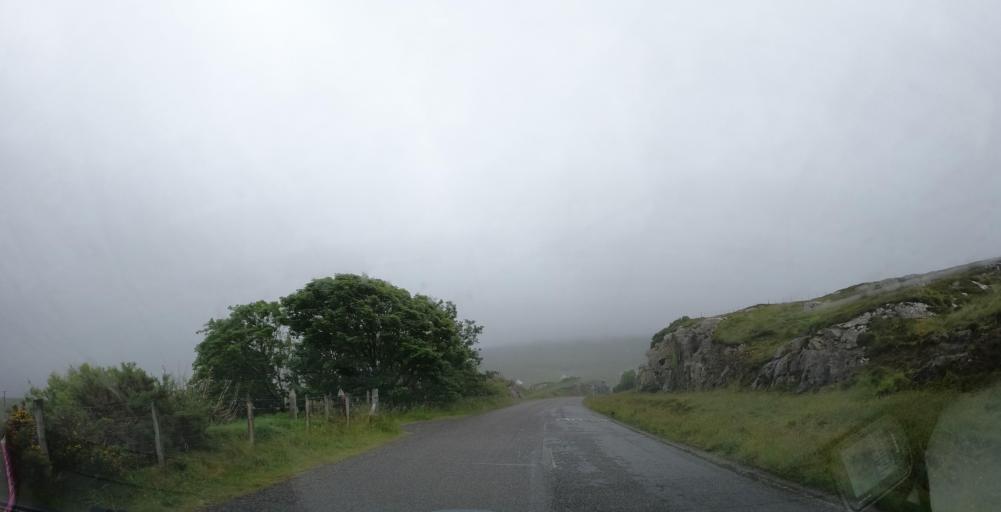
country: GB
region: Scotland
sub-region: Eilean Siar
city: Barra
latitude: 57.0048
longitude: -7.4278
